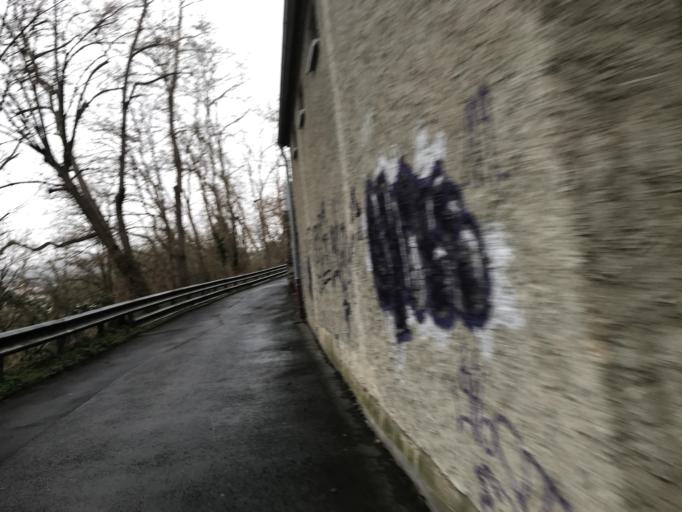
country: DE
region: Hesse
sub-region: Regierungsbezirk Kassel
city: Bad Wildungen
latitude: 51.1184
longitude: 9.1248
